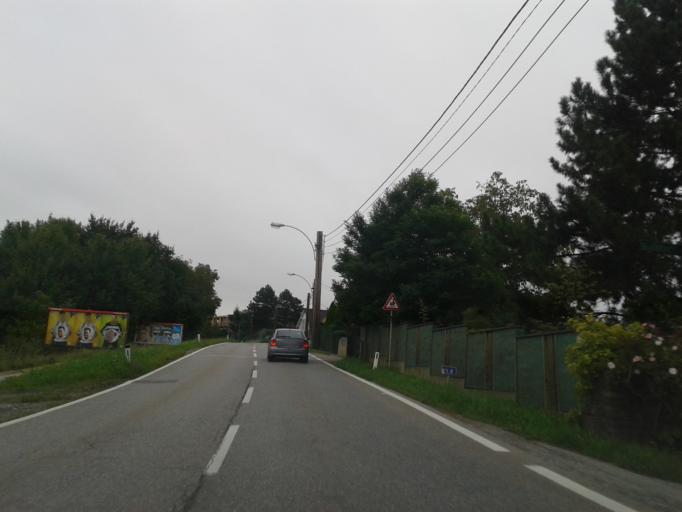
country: AT
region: Styria
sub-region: Graz Stadt
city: Mariatrost
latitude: 47.0846
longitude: 15.4845
